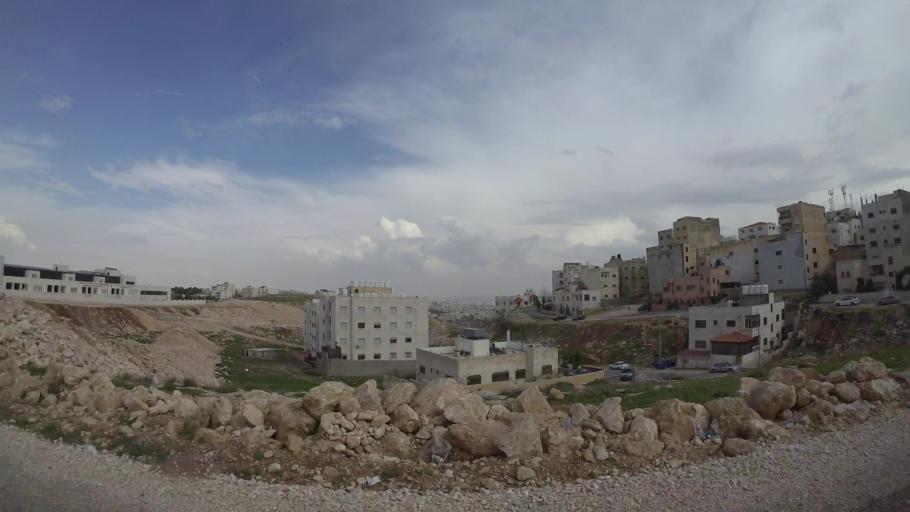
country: JO
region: Amman
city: Amman
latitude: 32.0151
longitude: 35.9429
